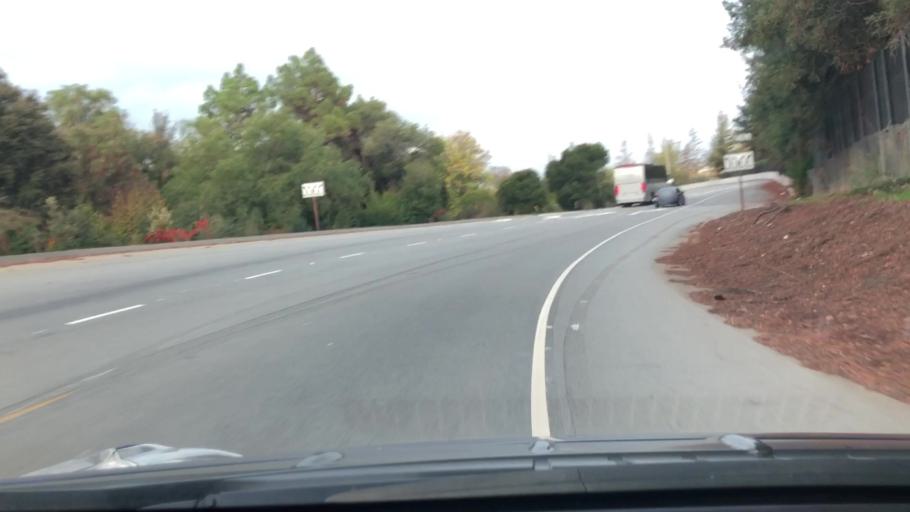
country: US
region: California
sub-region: Santa Clara County
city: Cupertino
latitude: 37.3302
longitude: -122.0127
